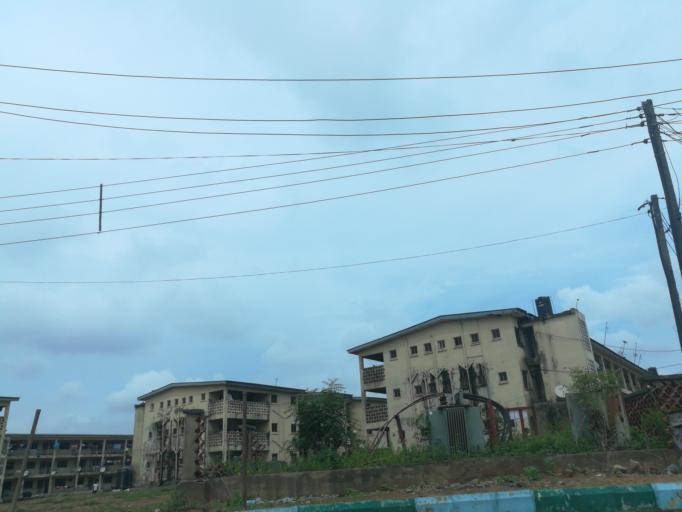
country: NG
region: Lagos
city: Ojota
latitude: 6.5713
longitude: 3.3610
